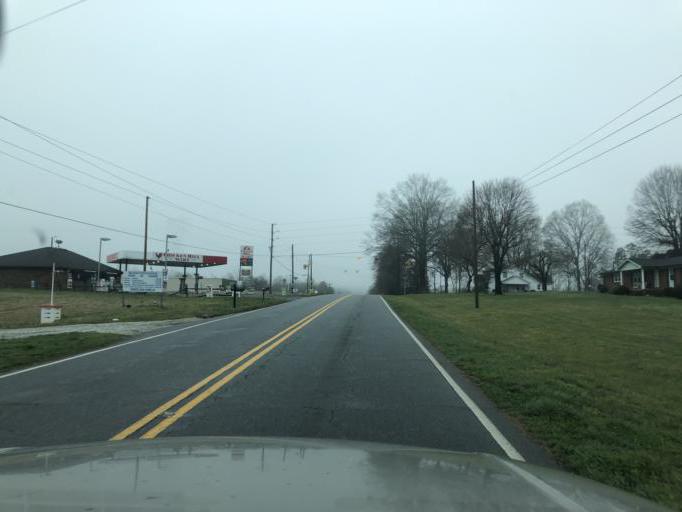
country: US
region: North Carolina
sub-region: Gaston County
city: Cherryville
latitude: 35.3485
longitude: -81.4472
